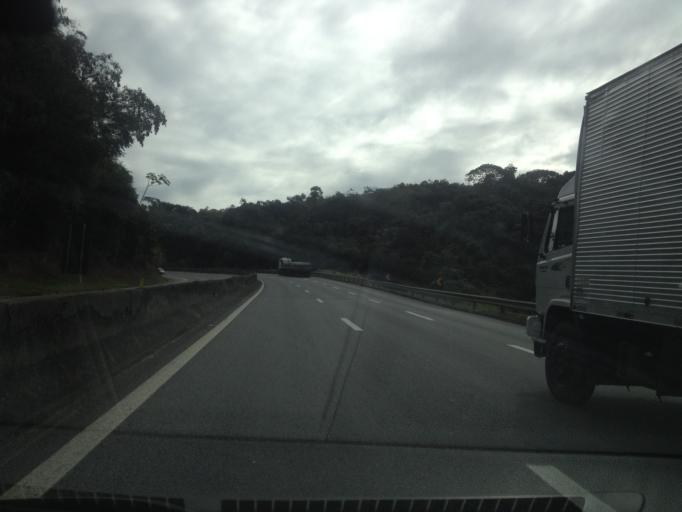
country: BR
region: Rio de Janeiro
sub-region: Pirai
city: Pirai
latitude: -22.6046
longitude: -43.9354
